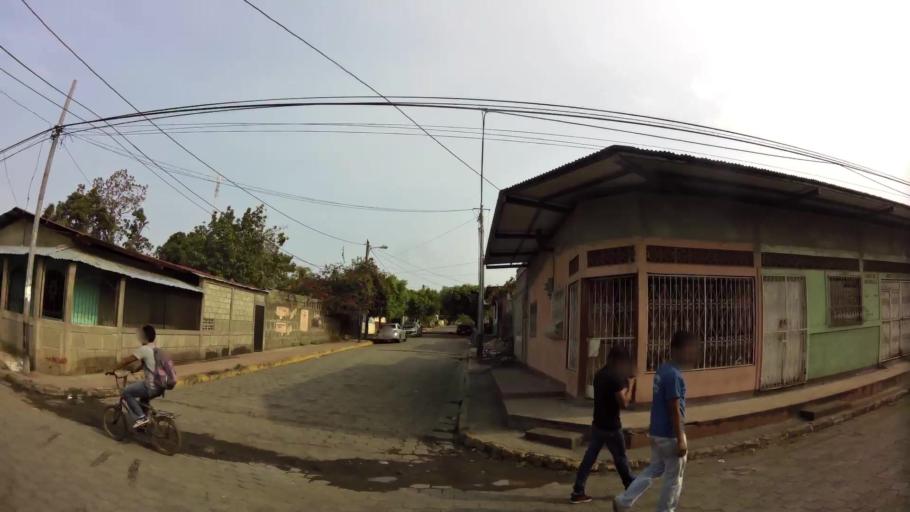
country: NI
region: Masaya
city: Masaya
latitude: 11.9681
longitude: -86.0910
